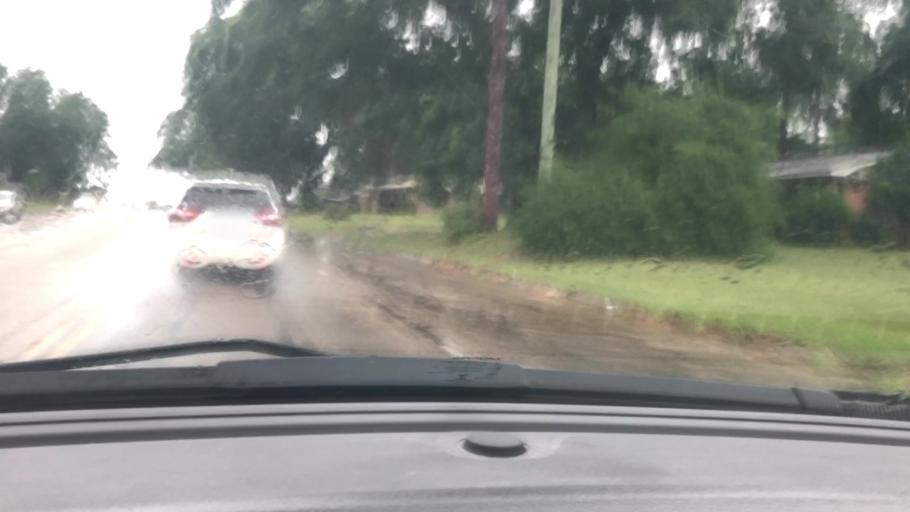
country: US
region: Texas
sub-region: Bowie County
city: Wake Village
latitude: 33.4491
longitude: -94.0801
